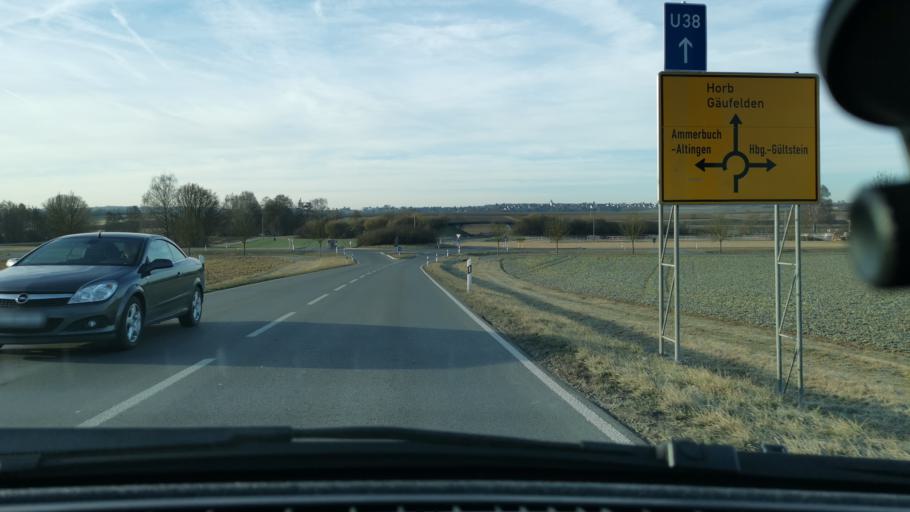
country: DE
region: Baden-Wuerttemberg
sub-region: Regierungsbezirk Stuttgart
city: Herrenberg
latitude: 48.5712
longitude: 8.8926
